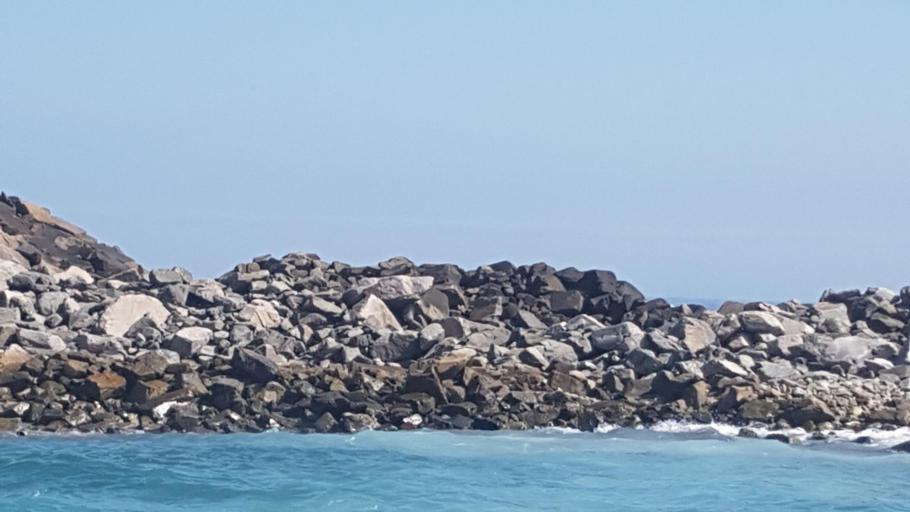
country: PE
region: Arequipa
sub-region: Provincia de Islay
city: Mollendo
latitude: -17.0308
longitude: -72.0166
